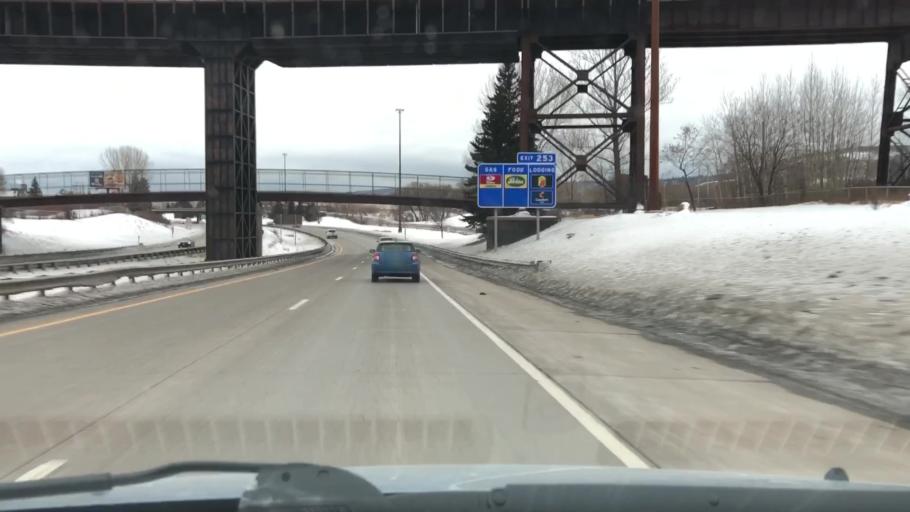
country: US
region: Minnesota
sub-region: Saint Louis County
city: Duluth
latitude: 46.7532
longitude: -92.1390
